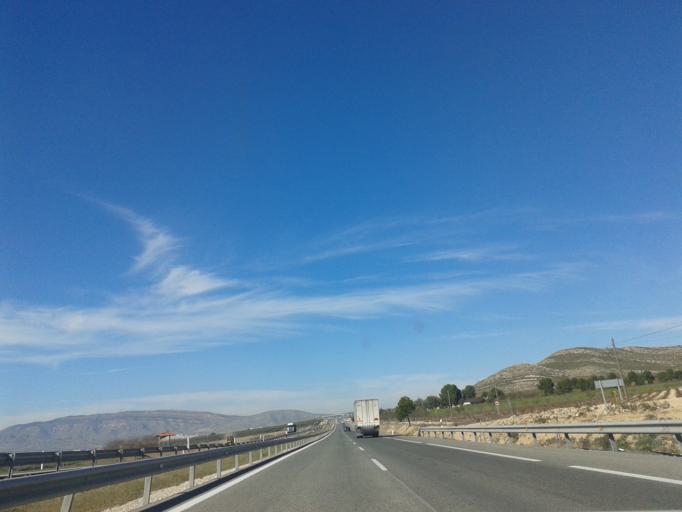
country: ES
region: Valencia
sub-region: Provincia de Alicante
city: Villena
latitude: 38.6862
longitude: -0.9045
